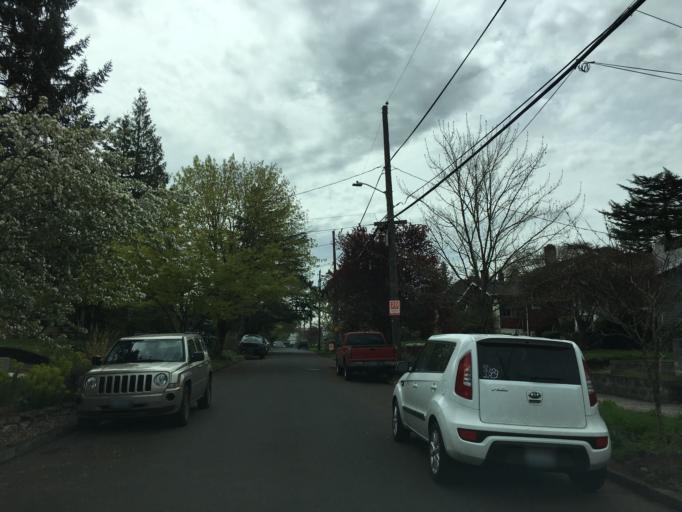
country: US
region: Oregon
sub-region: Multnomah County
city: Lents
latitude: 45.5476
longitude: -122.5879
